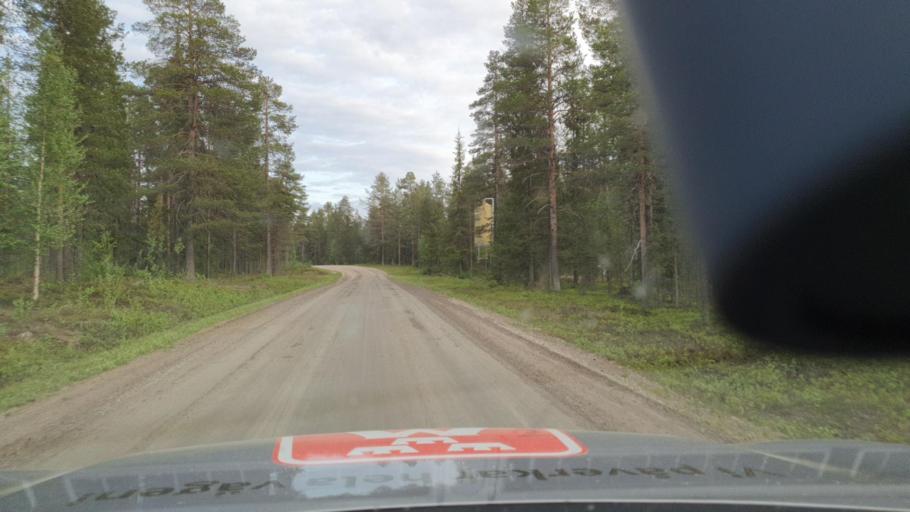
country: SE
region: Norrbotten
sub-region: Gallivare Kommun
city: Gaellivare
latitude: 66.6755
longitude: 21.2013
